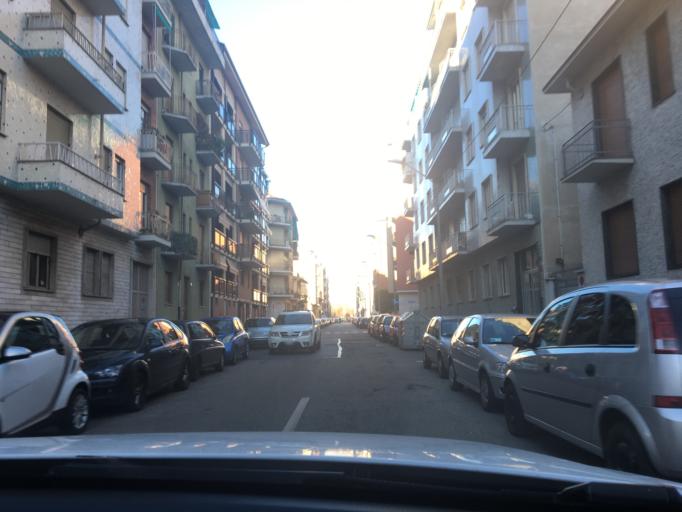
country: IT
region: Piedmont
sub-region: Provincia di Torino
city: Lesna
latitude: 45.0482
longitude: 7.6423
